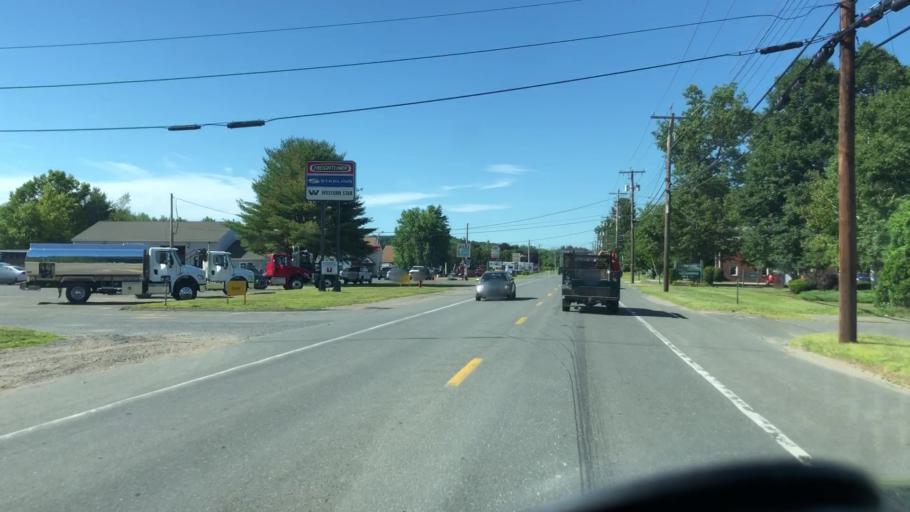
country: US
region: Massachusetts
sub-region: Hampden County
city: Westfield
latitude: 42.1704
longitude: -72.7268
